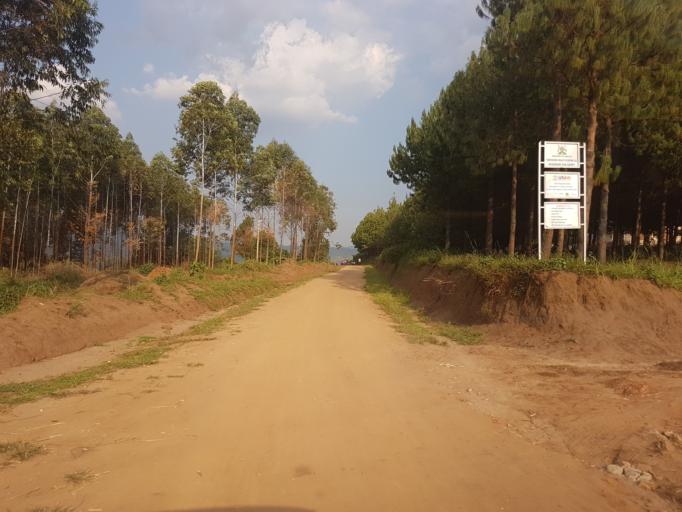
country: UG
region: Western Region
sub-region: Rukungiri District
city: Rukungiri
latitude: -0.6647
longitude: 29.8768
